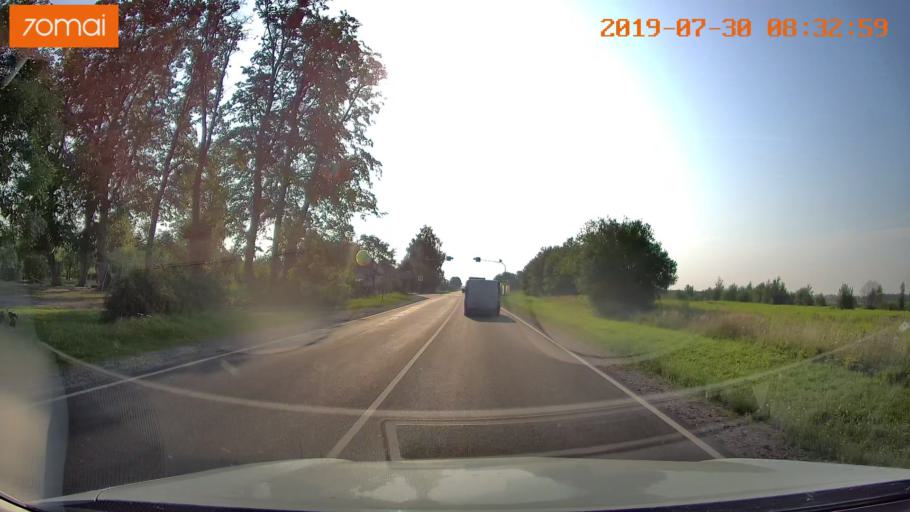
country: RU
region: Kaliningrad
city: Chernyakhovsk
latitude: 54.6366
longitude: 21.7380
